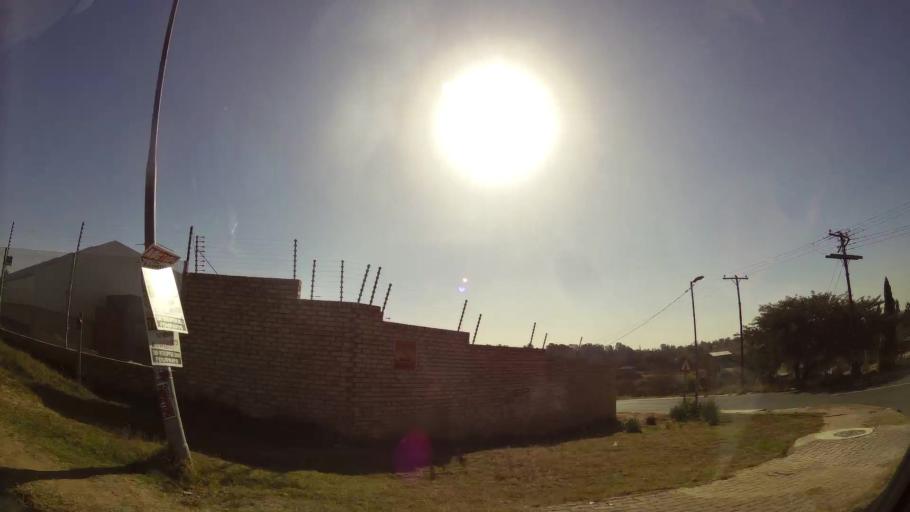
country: ZA
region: Gauteng
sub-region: City of Johannesburg Metropolitan Municipality
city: Diepsloot
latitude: -26.0091
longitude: 27.9472
